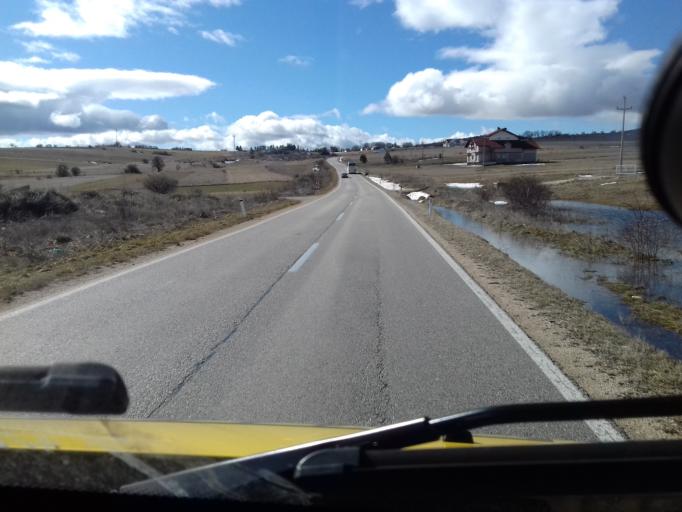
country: BA
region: Federation of Bosnia and Herzegovina
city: Tomislavgrad
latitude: 43.7428
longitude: 17.2257
